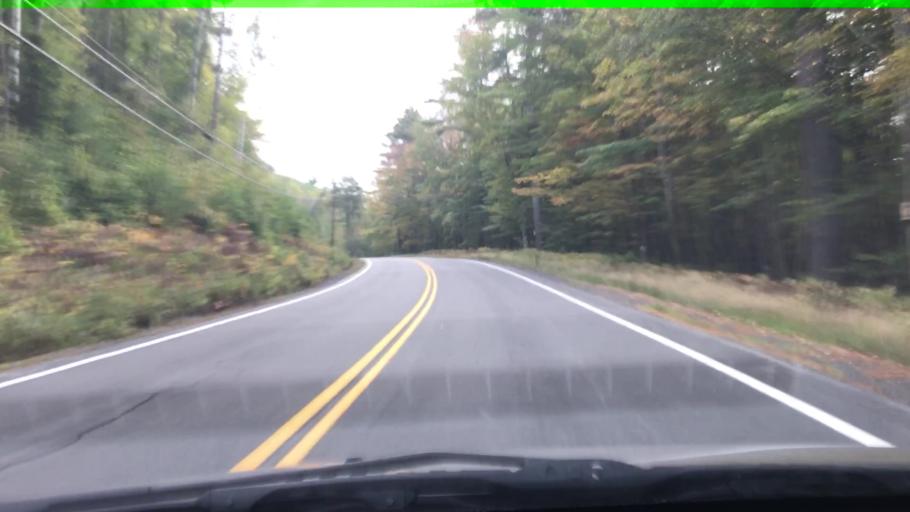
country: US
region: New Hampshire
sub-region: Sullivan County
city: Lempster
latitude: 43.0987
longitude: -72.1611
